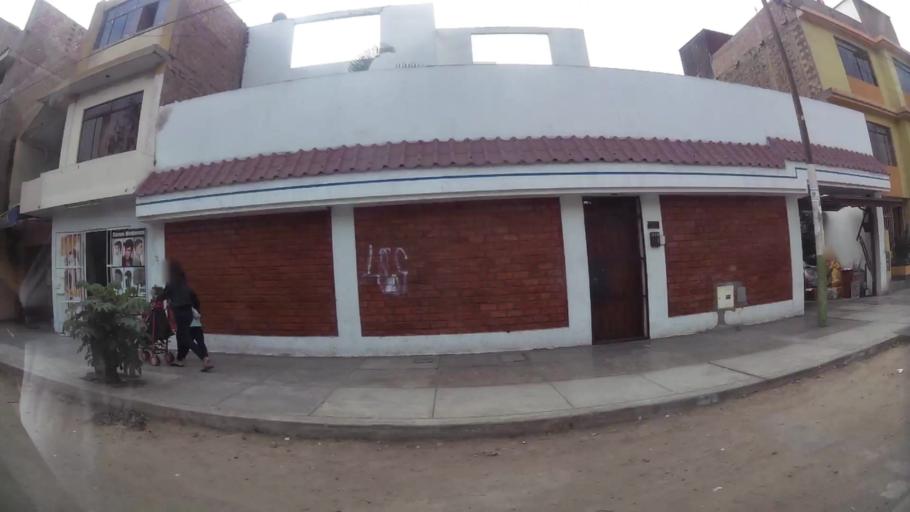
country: PE
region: Callao
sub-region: Callao
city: Callao
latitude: -12.0177
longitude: -77.0943
